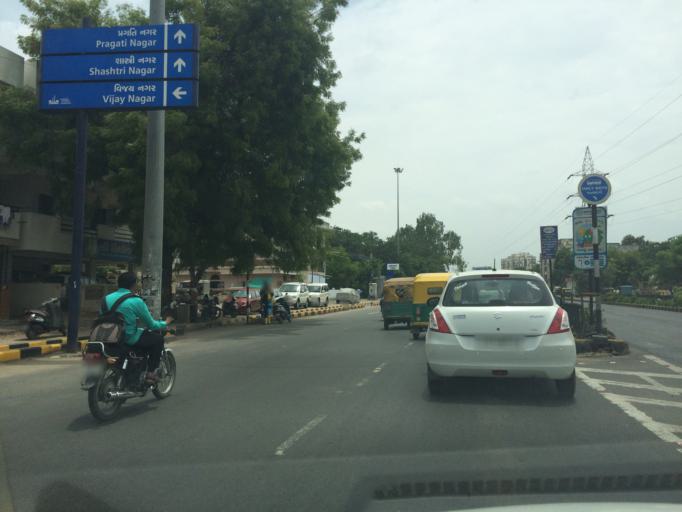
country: IN
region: Gujarat
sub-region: Ahmadabad
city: Ahmedabad
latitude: 23.0656
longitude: 72.5578
